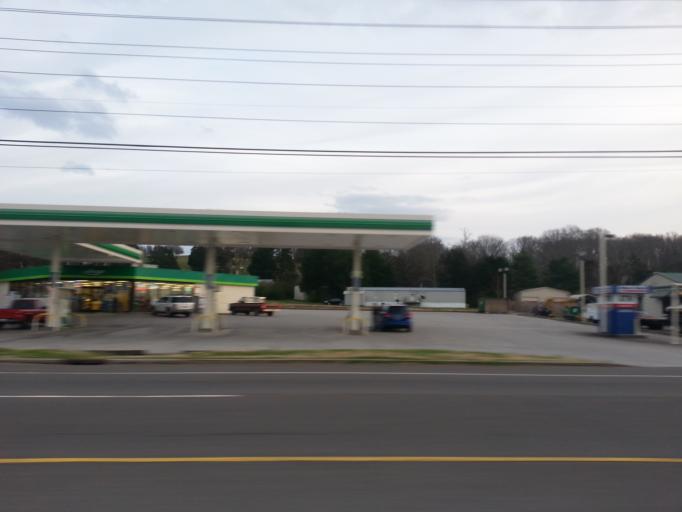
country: US
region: Tennessee
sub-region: Monroe County
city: Madisonville
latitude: 35.5305
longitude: -84.3426
